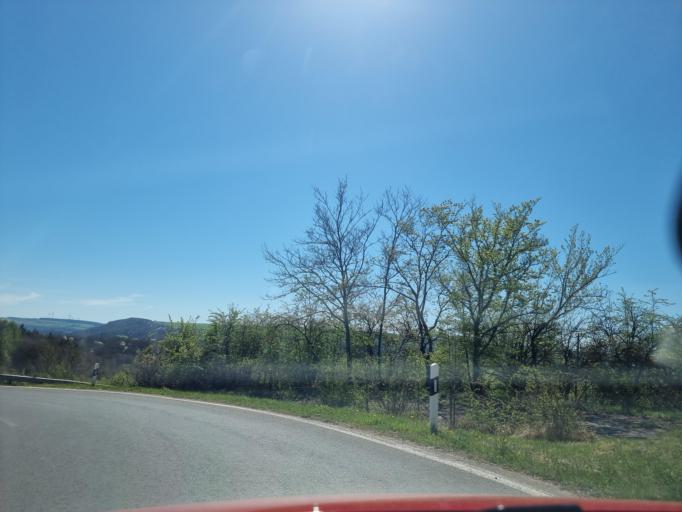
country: DE
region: Rheinland-Pfalz
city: Echternacherbruck
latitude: 49.8299
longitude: 6.4453
